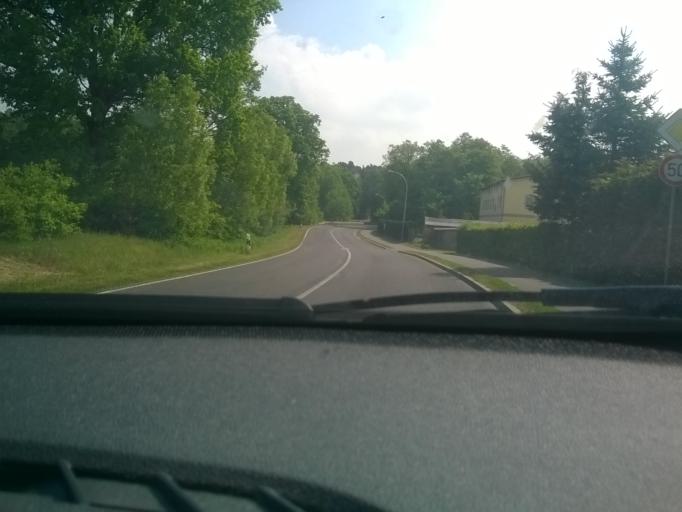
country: DE
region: Brandenburg
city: Wittstock
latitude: 53.1876
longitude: 12.4944
